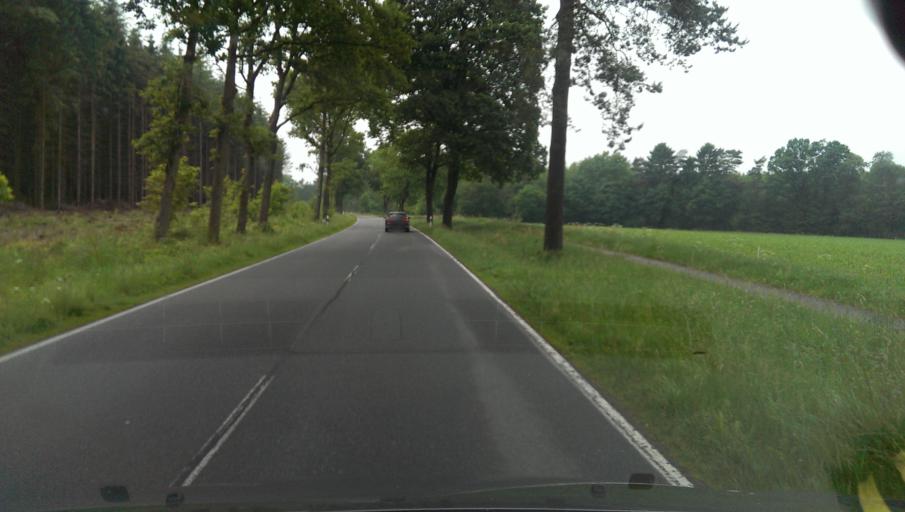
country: DE
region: Lower Saxony
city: Fassberg
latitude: 52.8882
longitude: 10.1745
